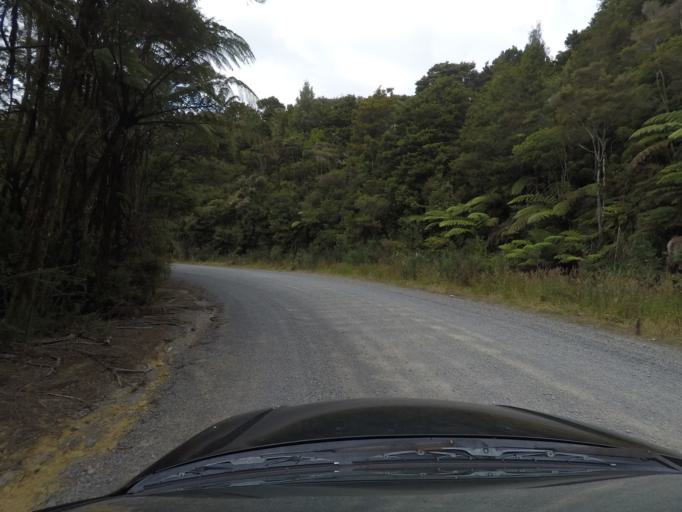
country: NZ
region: Northland
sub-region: Whangarei
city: Ruakaka
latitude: -35.9266
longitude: 174.3380
